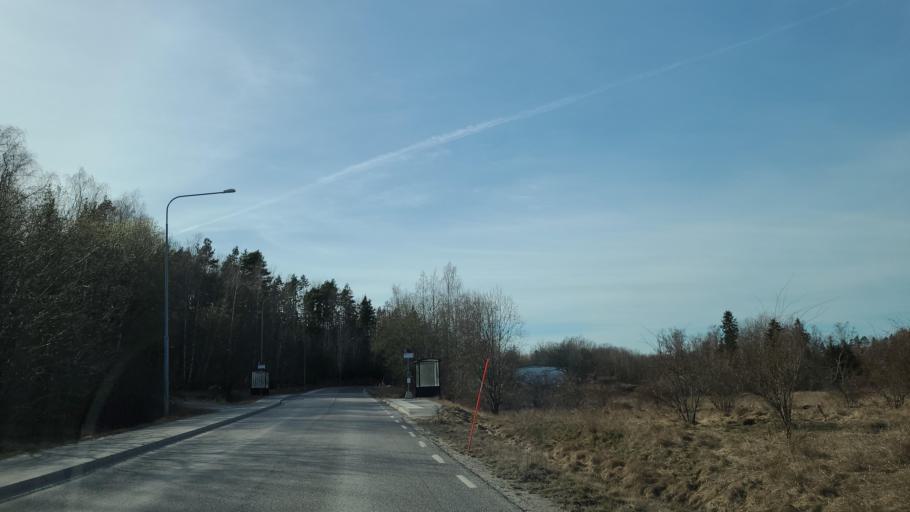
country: SE
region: Stockholm
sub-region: Ekero Kommun
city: Ekeroe
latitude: 59.2800
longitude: 17.7768
